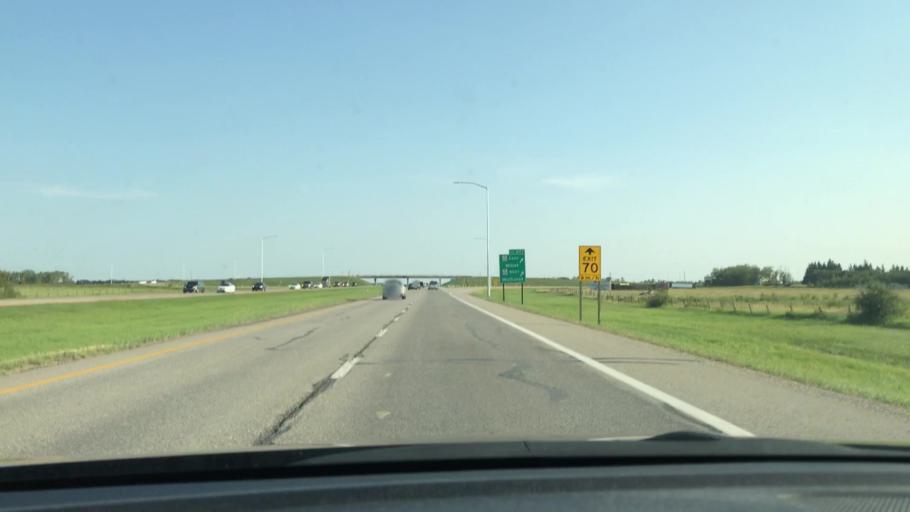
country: CA
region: Alberta
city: Millet
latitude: 53.0962
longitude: -113.5983
